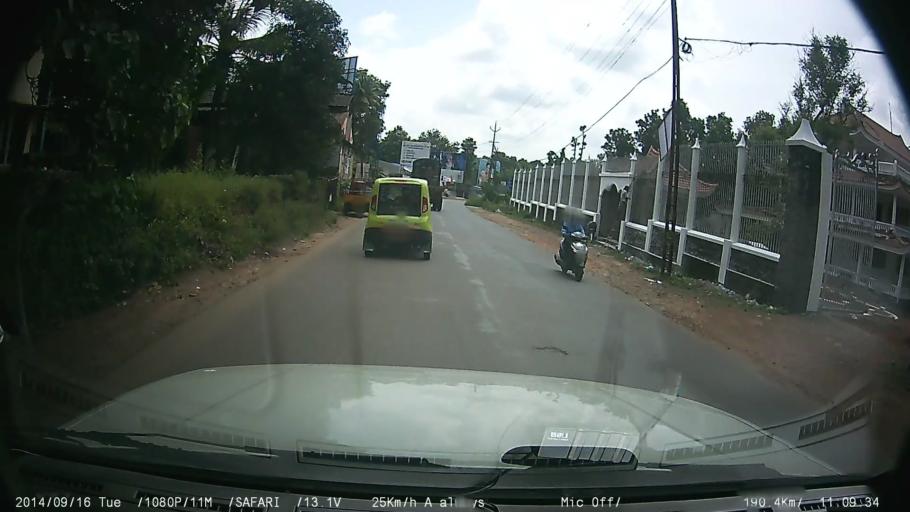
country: IN
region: Kerala
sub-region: Kottayam
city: Kottayam
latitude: 9.5260
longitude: 76.5226
